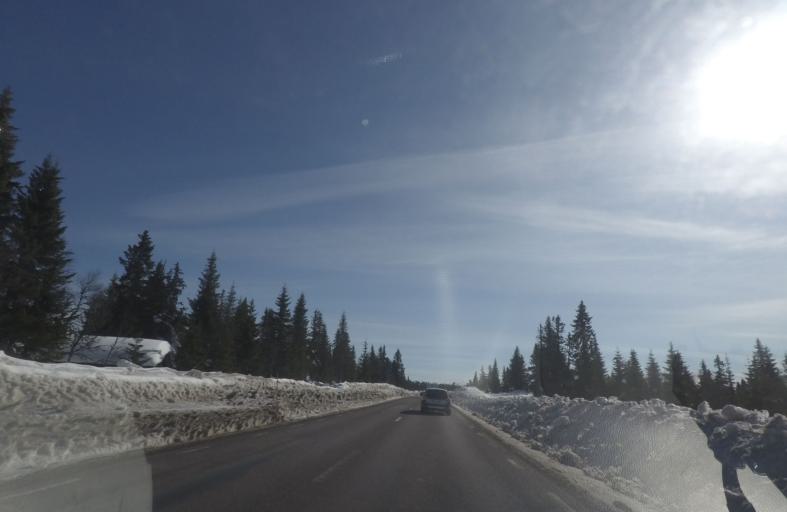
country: SE
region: Dalarna
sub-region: Malung-Saelens kommun
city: Malung
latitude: 61.1651
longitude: 13.1012
